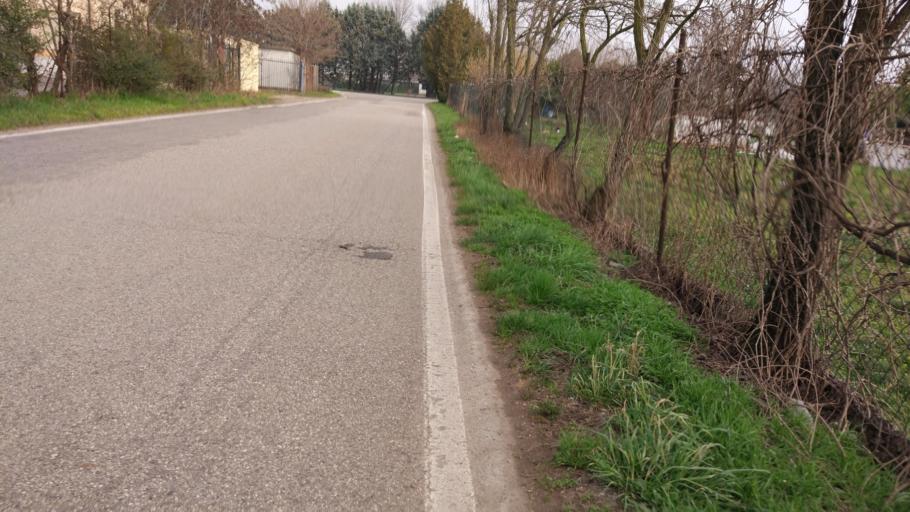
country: IT
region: Veneto
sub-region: Provincia di Verona
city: Dossobuono
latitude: 45.3826
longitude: 10.8773
